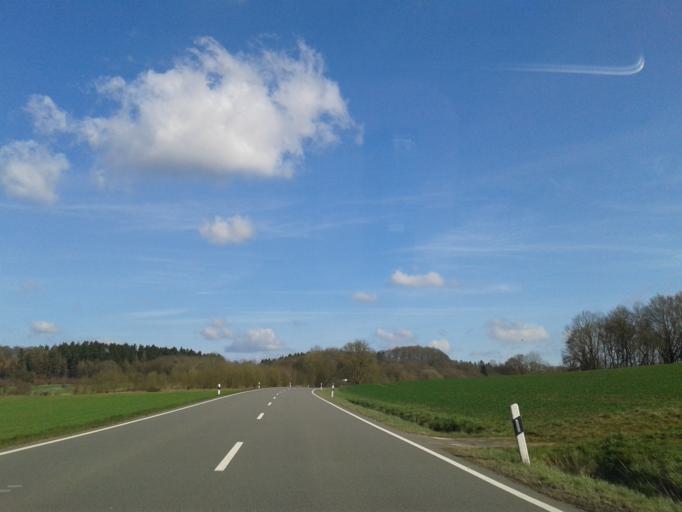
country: DE
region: Hesse
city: Allendorf
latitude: 51.0030
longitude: 8.6847
